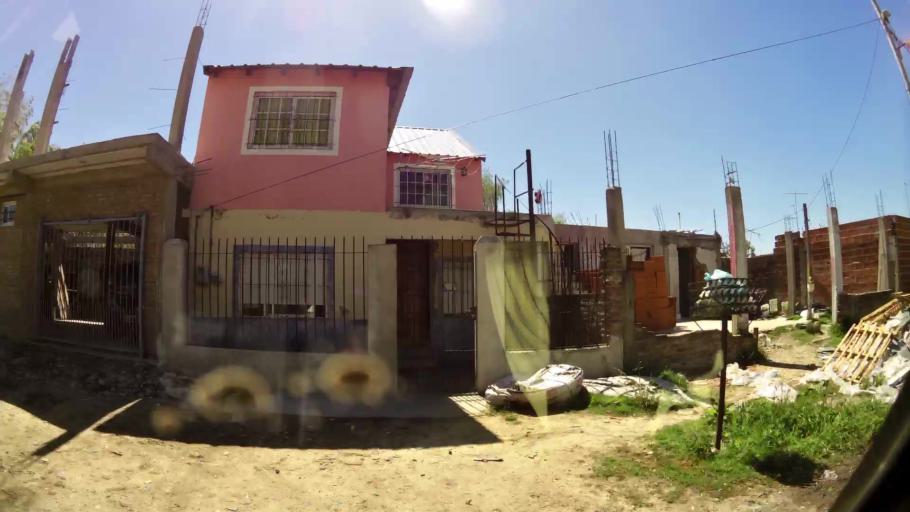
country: AR
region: Buenos Aires
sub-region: Partido de Quilmes
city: Quilmes
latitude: -34.7295
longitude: -58.3129
